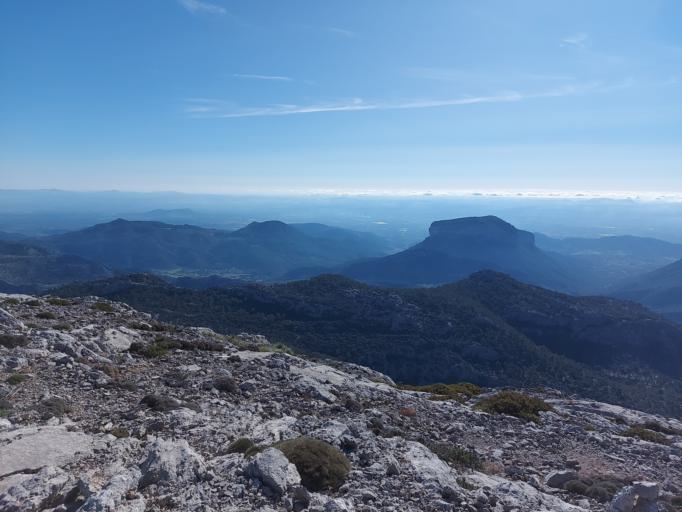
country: ES
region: Balearic Islands
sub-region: Illes Balears
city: Fornalutx
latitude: 39.7713
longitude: 2.7833
